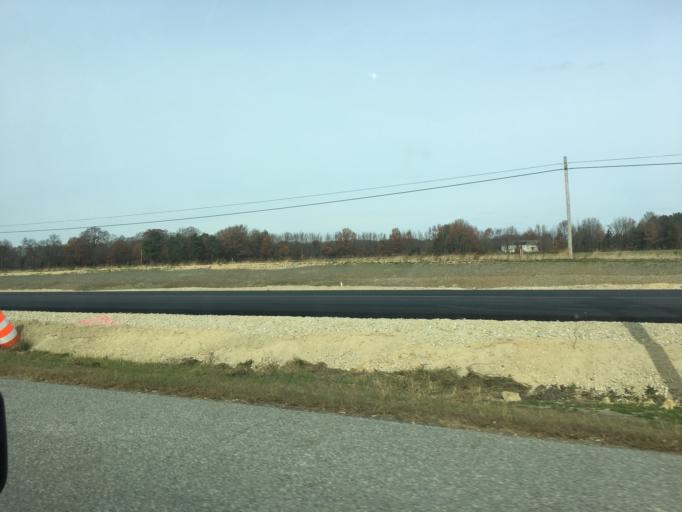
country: US
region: Maryland
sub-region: Queen Anne's County
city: Centreville
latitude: 38.9313
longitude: -76.0188
